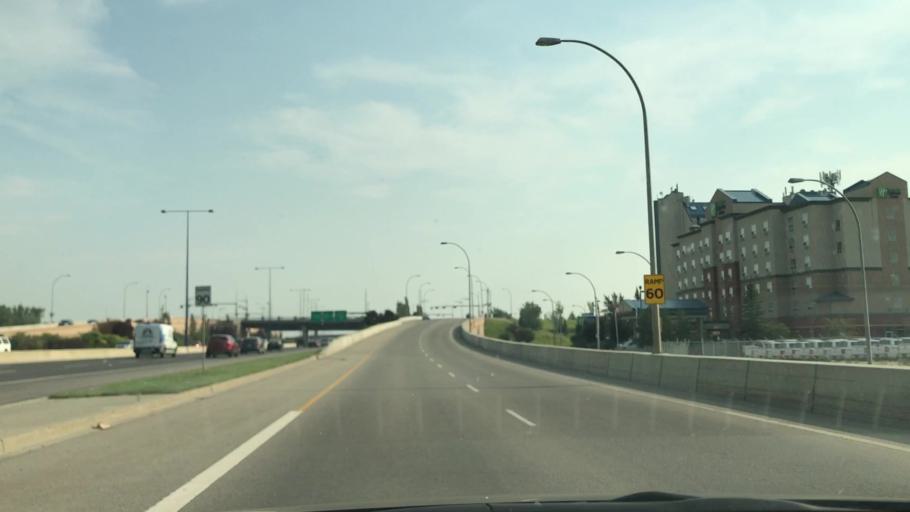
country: CA
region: Alberta
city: Edmonton
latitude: 53.4572
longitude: -113.4927
